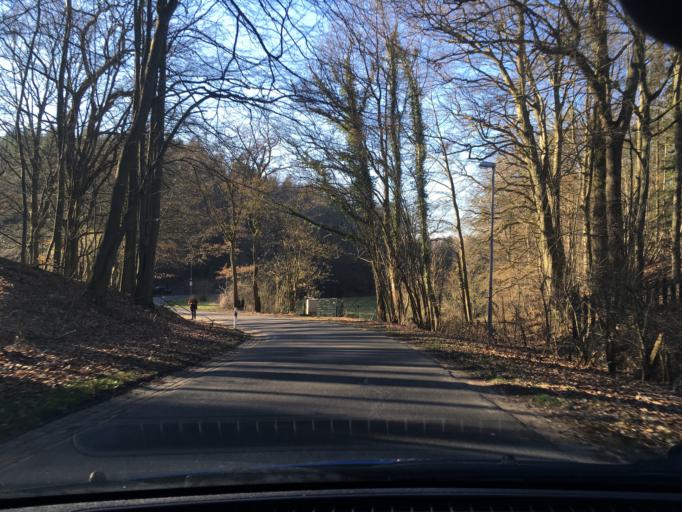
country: DE
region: Schleswig-Holstein
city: Schnakenbek
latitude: 53.3770
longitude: 10.5137
